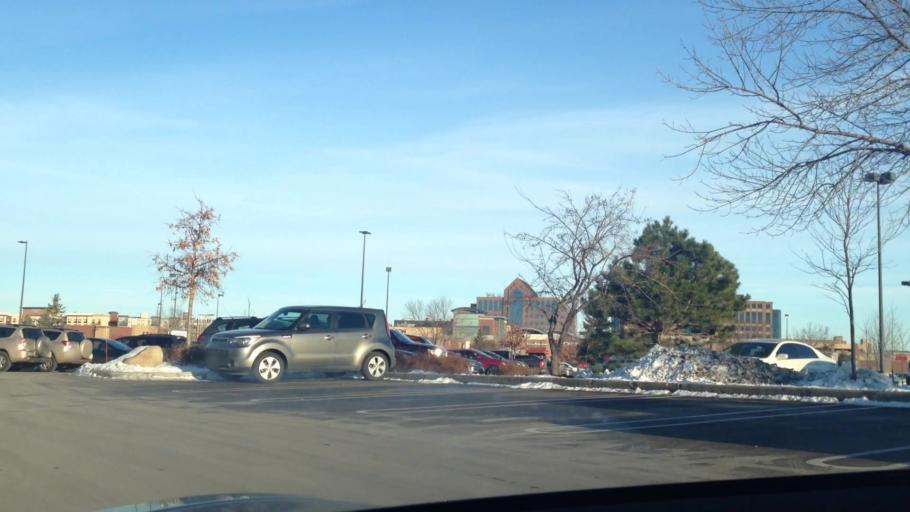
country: US
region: Minnesota
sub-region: Hennepin County
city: Saint Louis Park
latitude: 44.9662
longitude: -93.3529
